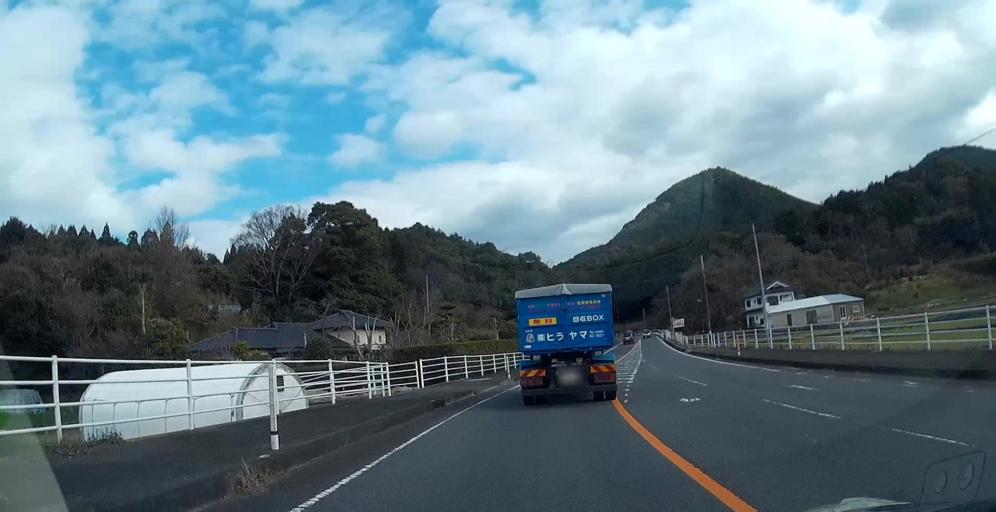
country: JP
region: Kumamoto
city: Minamata
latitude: 32.2259
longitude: 130.4386
